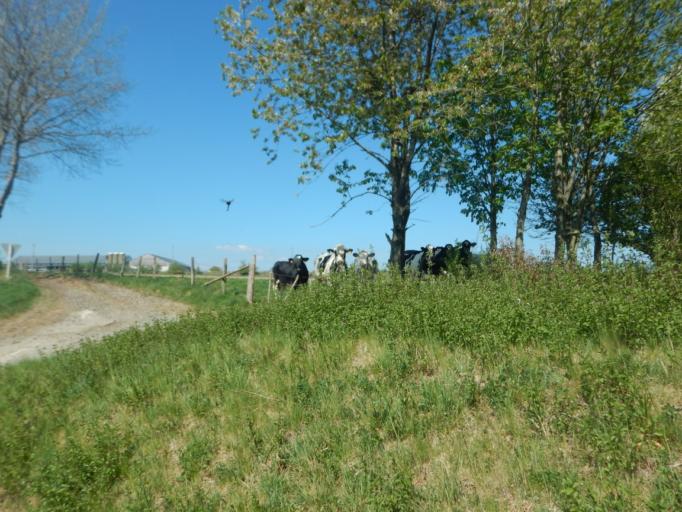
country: LU
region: Diekirch
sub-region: Canton de Clervaux
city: Troisvierges
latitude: 50.1558
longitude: 5.9868
